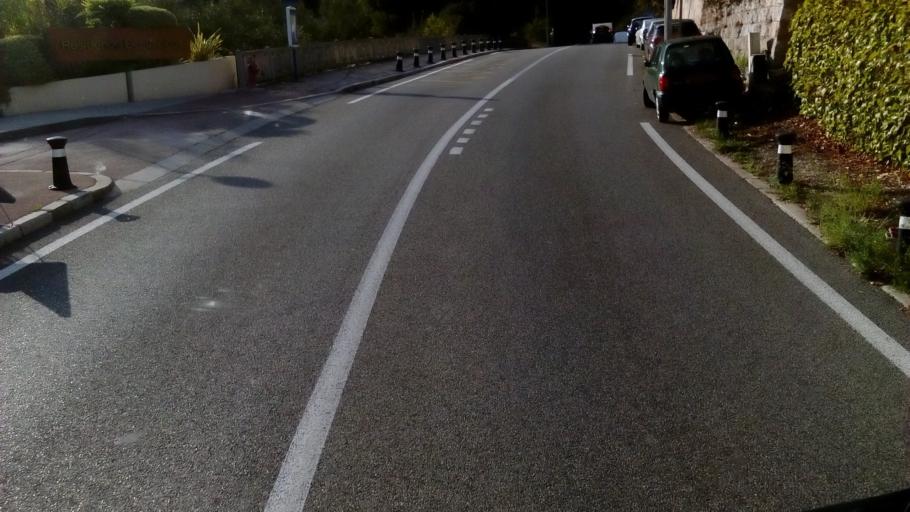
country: MC
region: Commune de Monaco
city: Saint-Roman
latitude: 43.7517
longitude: 7.4276
